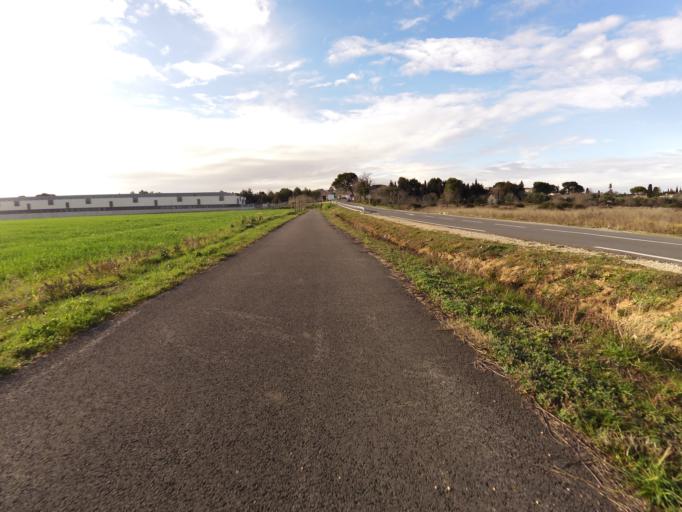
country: FR
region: Languedoc-Roussillon
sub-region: Departement du Gard
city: Gallargues-le-Montueux
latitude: 43.7178
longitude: 4.1793
